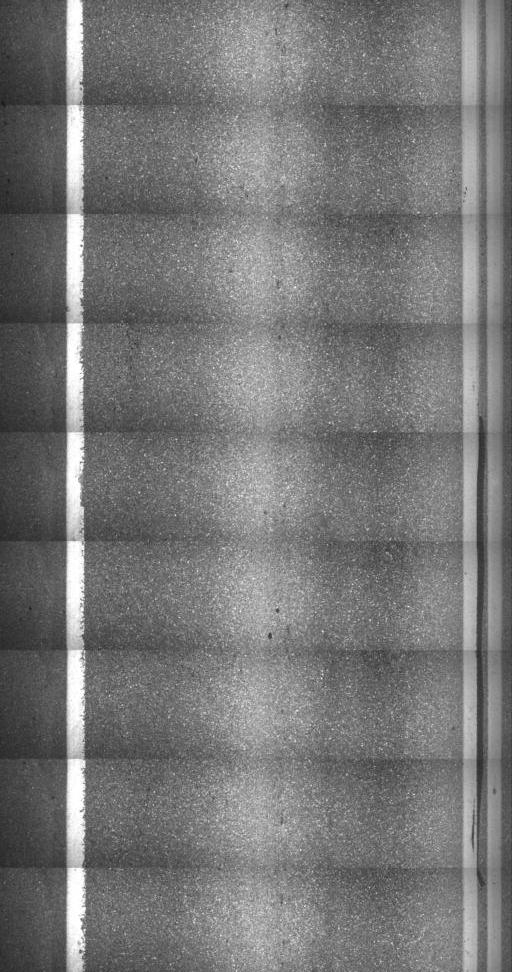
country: US
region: Vermont
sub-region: Chittenden County
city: Hinesburg
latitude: 44.3709
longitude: -73.1299
